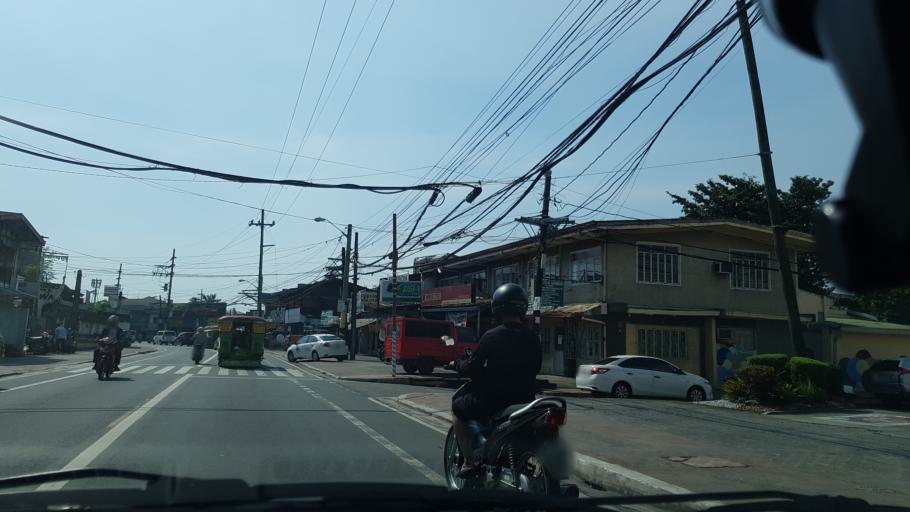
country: PH
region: Metro Manila
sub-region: Marikina
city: Calumpang
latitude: 14.6494
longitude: 121.1002
